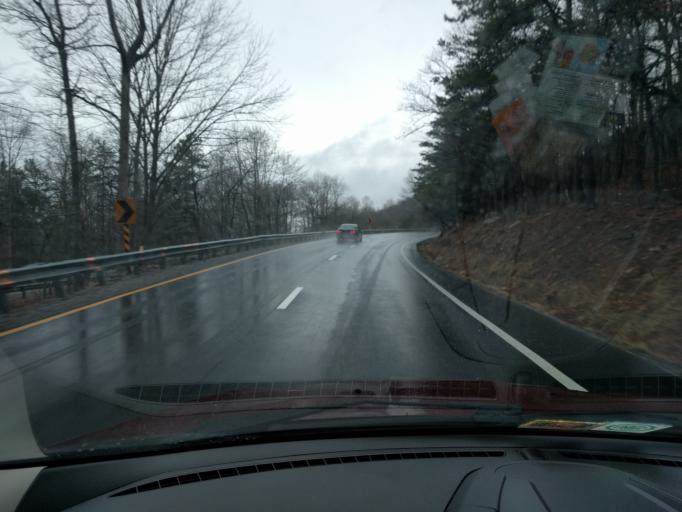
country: US
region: Virginia
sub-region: Montgomery County
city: Prices Fork
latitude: 37.2858
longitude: -80.4719
